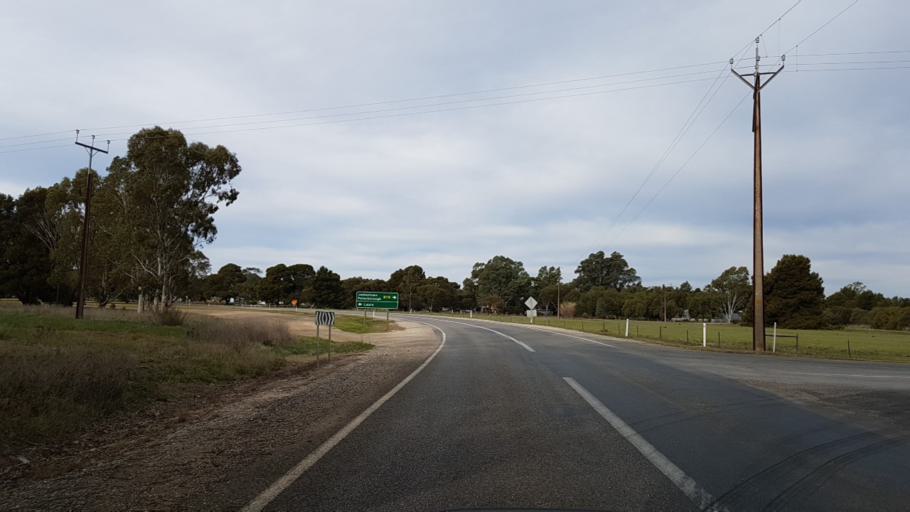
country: AU
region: South Australia
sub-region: Northern Areas
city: Jamestown
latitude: -33.1821
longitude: 138.4773
